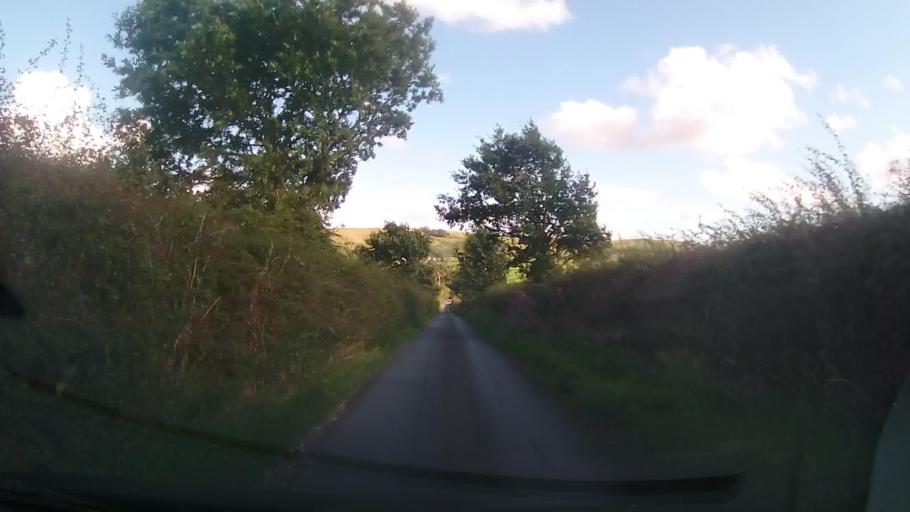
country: GB
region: England
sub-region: Shropshire
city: Norbury
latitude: 52.5646
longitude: -2.8997
